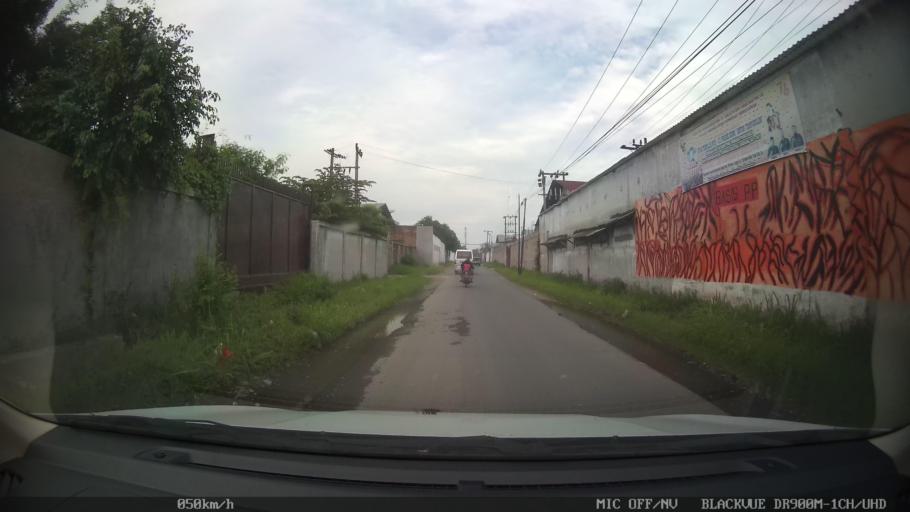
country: ID
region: North Sumatra
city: Sunggal
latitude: 3.6144
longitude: 98.5890
